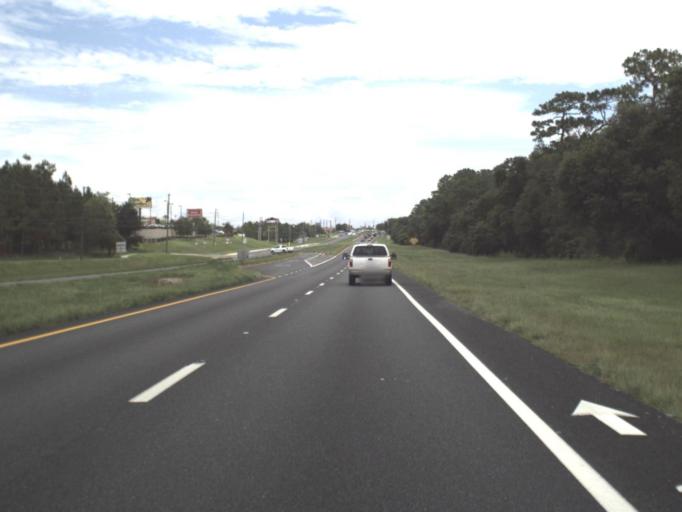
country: US
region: Florida
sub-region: Citrus County
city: Inverness Highlands North
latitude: 28.8556
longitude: -82.4007
